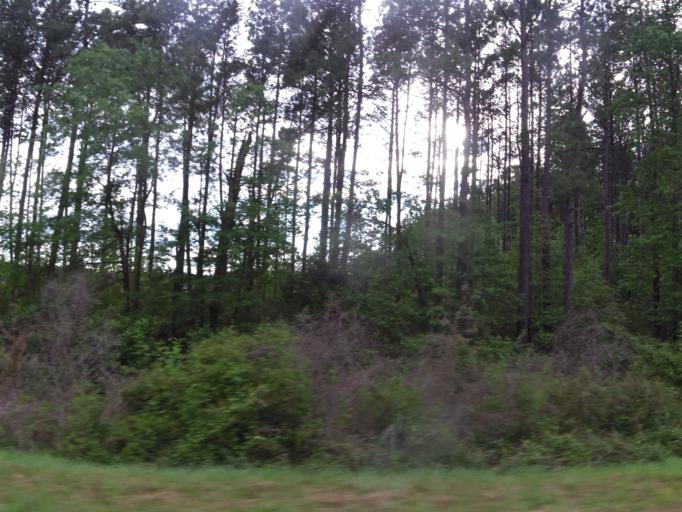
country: US
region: South Carolina
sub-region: Jasper County
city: Hardeeville
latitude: 32.3964
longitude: -81.0990
